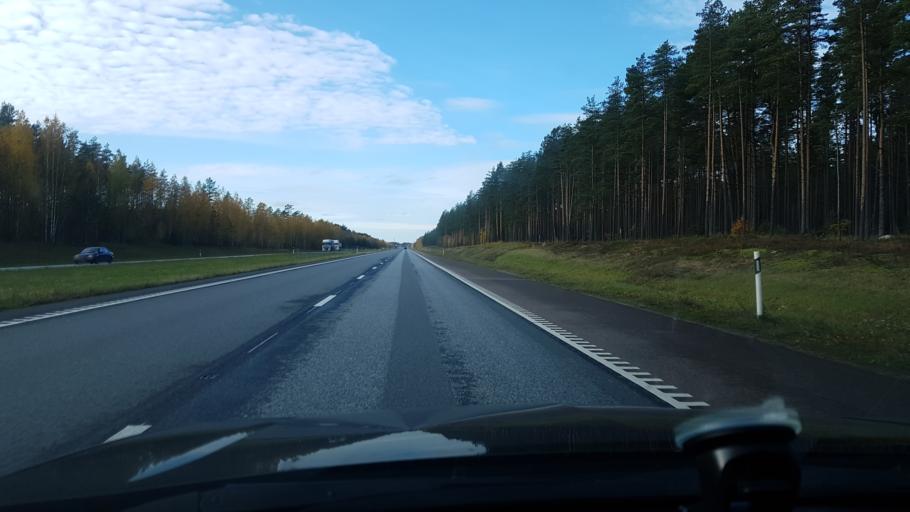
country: EE
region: Harju
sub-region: Kuusalu vald
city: Kuusalu
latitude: 59.4544
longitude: 25.4951
